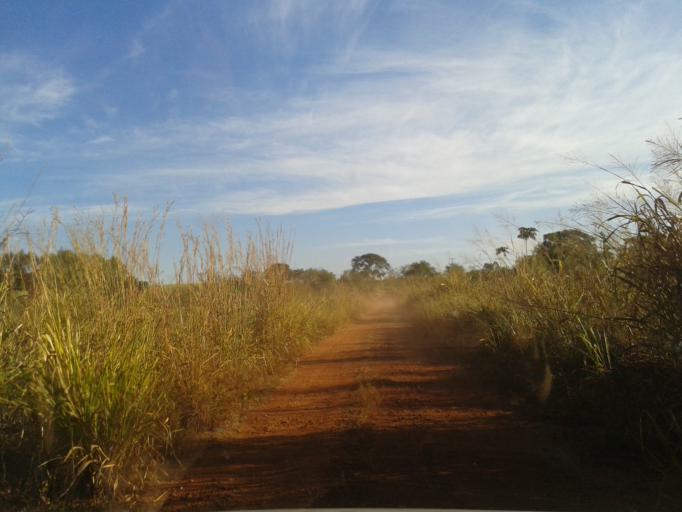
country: BR
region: Minas Gerais
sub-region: Santa Vitoria
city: Santa Vitoria
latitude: -18.9971
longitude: -50.3775
